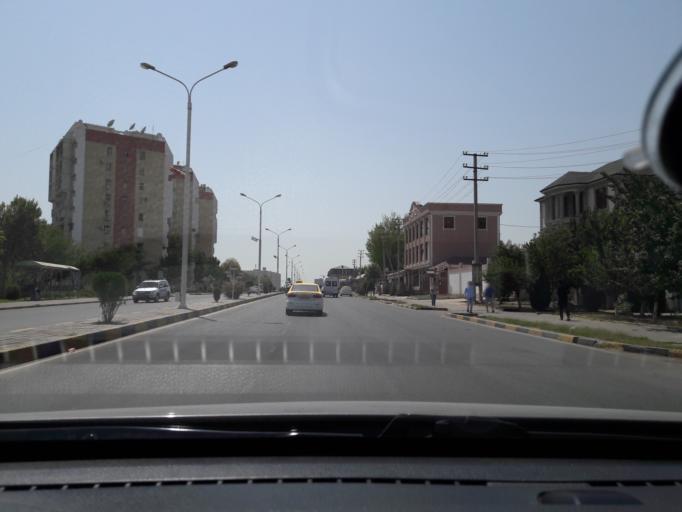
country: TJ
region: Dushanbe
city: Dushanbe
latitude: 38.5916
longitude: 68.7391
